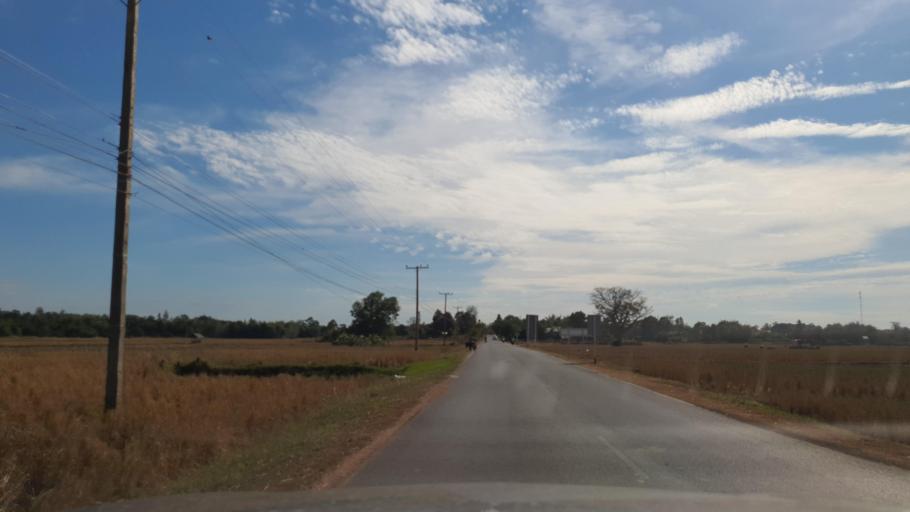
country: TH
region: Kalasin
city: Kuchinarai
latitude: 16.5527
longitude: 104.0974
